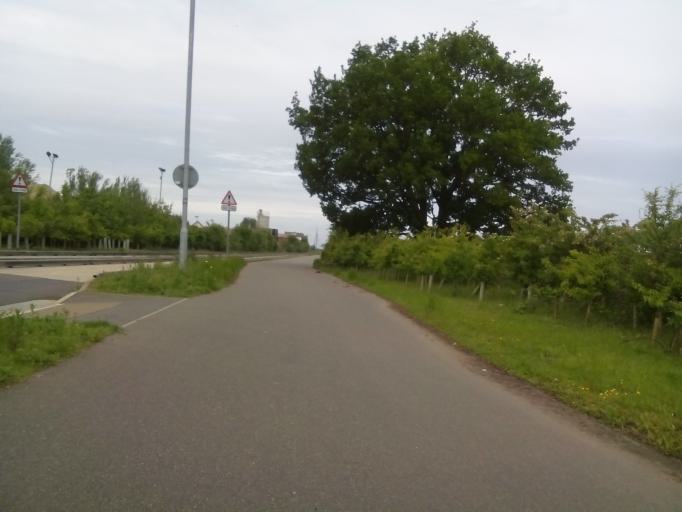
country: GB
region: England
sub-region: Cambridgeshire
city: Swavesey
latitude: 52.2920
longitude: 0.0541
